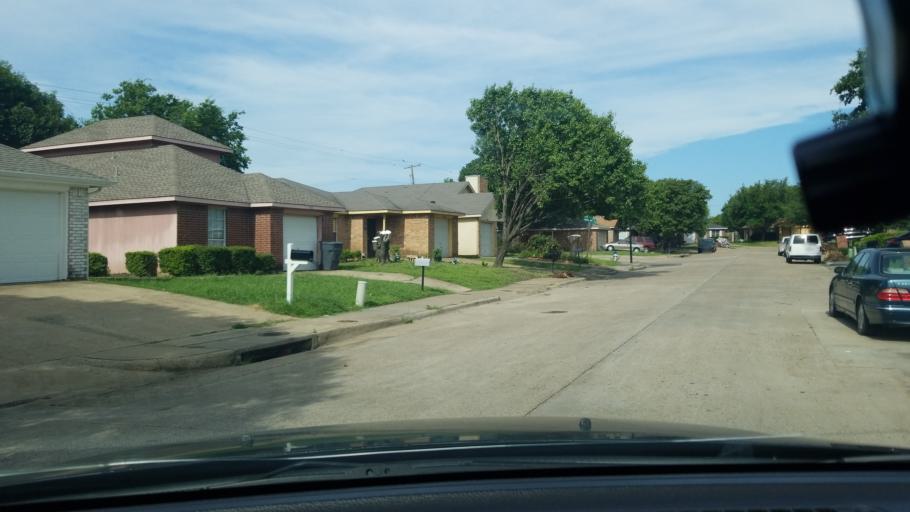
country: US
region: Texas
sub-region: Dallas County
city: Balch Springs
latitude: 32.7690
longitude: -96.6595
